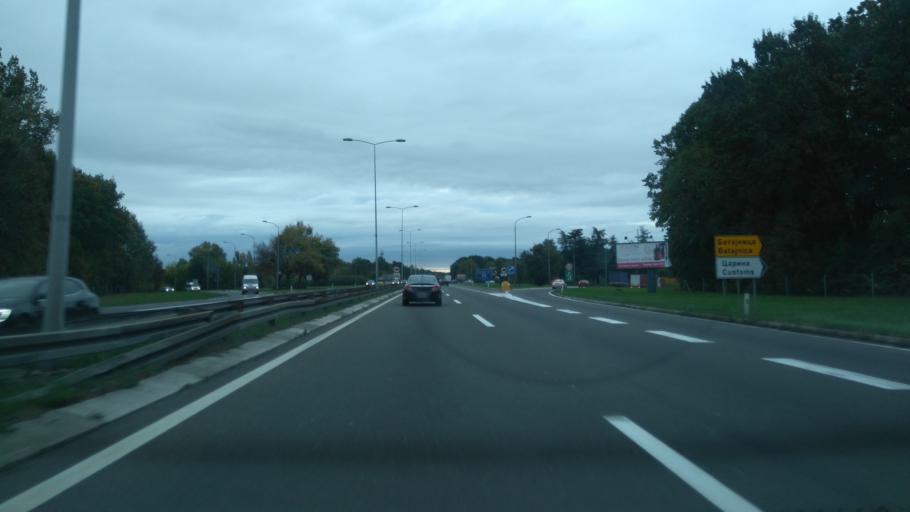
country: RS
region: Central Serbia
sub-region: Belgrade
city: Zemun
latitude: 44.8326
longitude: 20.3593
